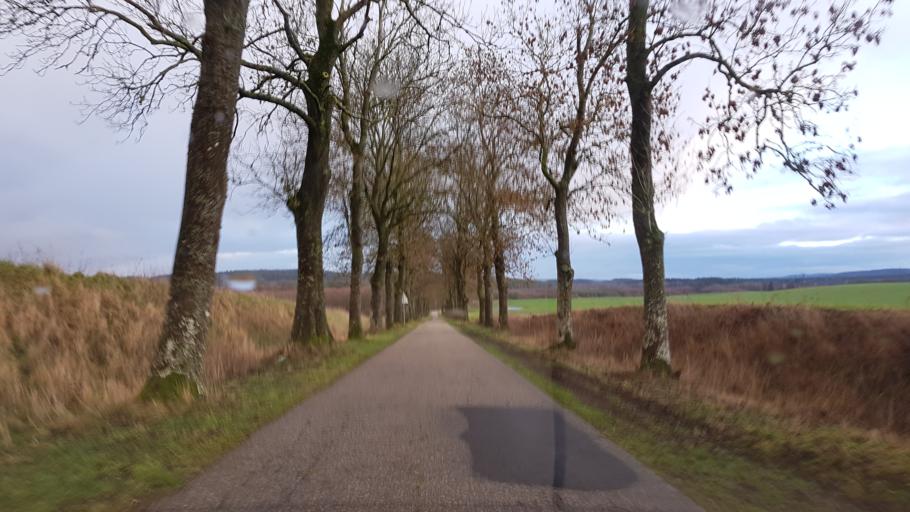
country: PL
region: West Pomeranian Voivodeship
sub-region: Powiat swidwinski
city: Rabino
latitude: 53.9432
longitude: 15.9296
